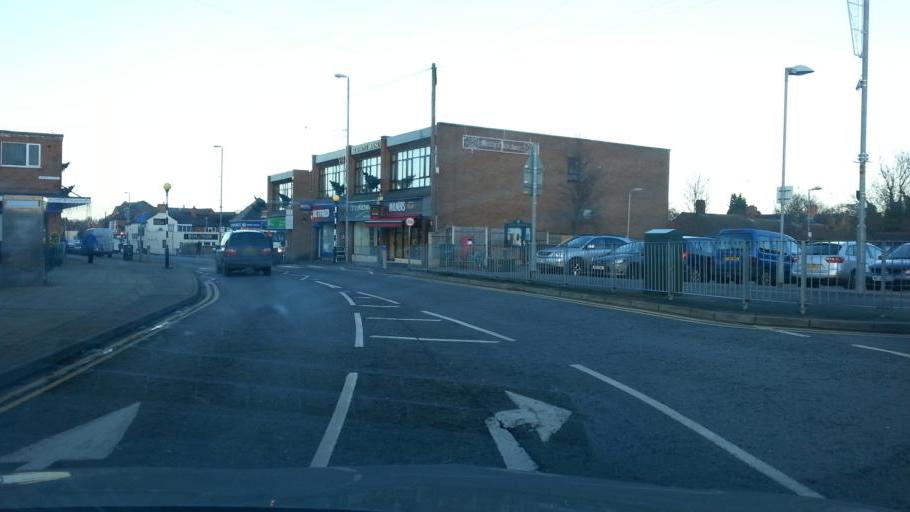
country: GB
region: England
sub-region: Leicestershire
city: Blaby
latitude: 52.5745
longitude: -1.1635
